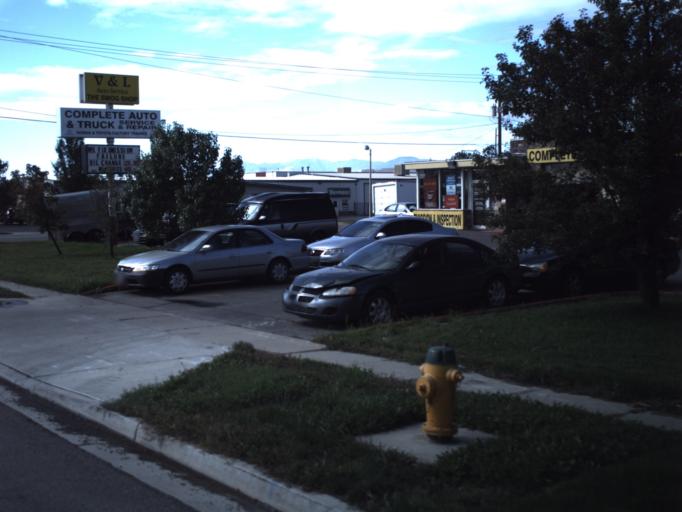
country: US
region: Utah
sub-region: Salt Lake County
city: Salt Lake City
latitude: 40.7518
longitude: -111.9391
